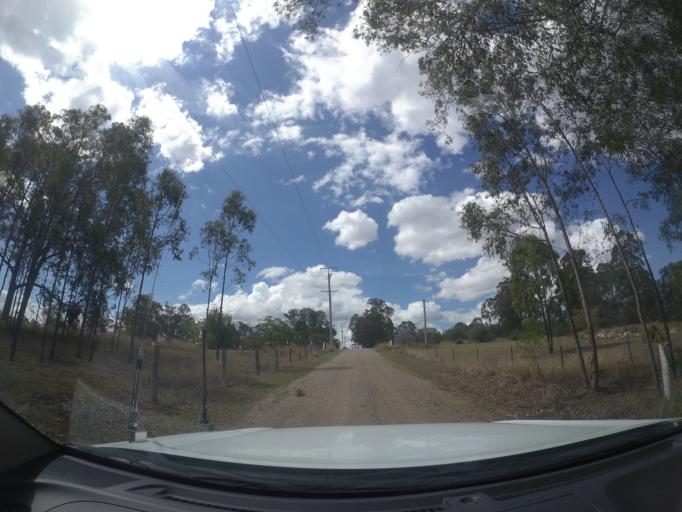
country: AU
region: Queensland
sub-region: Logan
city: Cedar Vale
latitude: -27.8975
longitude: 153.0010
